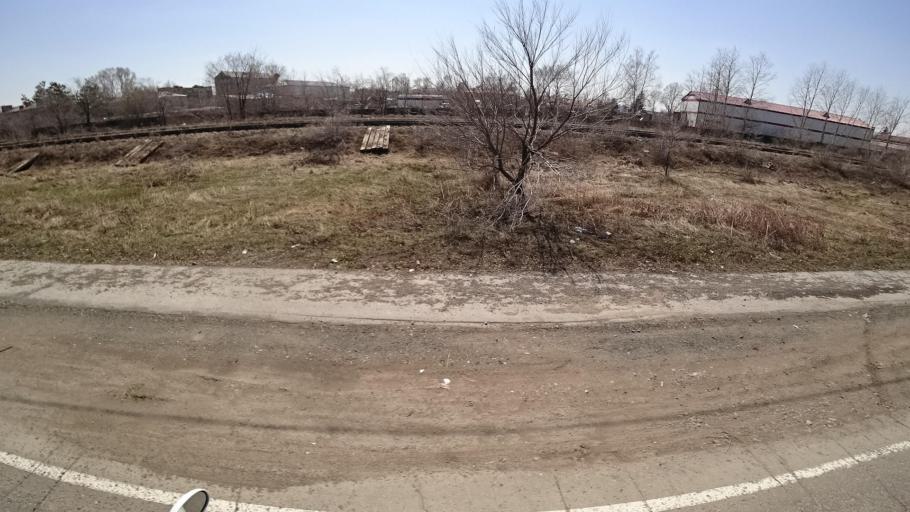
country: RU
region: Khabarovsk Krai
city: Khurba
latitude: 50.4085
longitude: 136.8913
